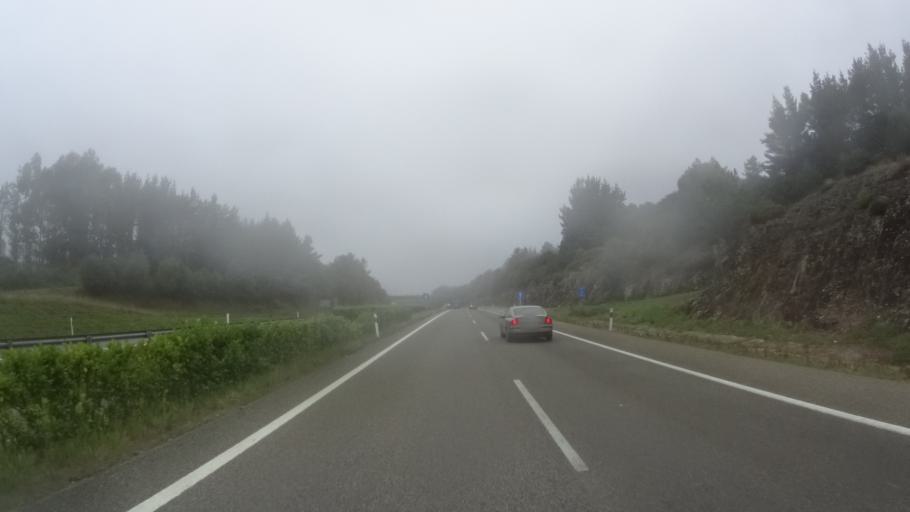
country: ES
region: Galicia
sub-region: Provincia de Lugo
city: Guitiriz
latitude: 43.1904
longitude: -7.8965
